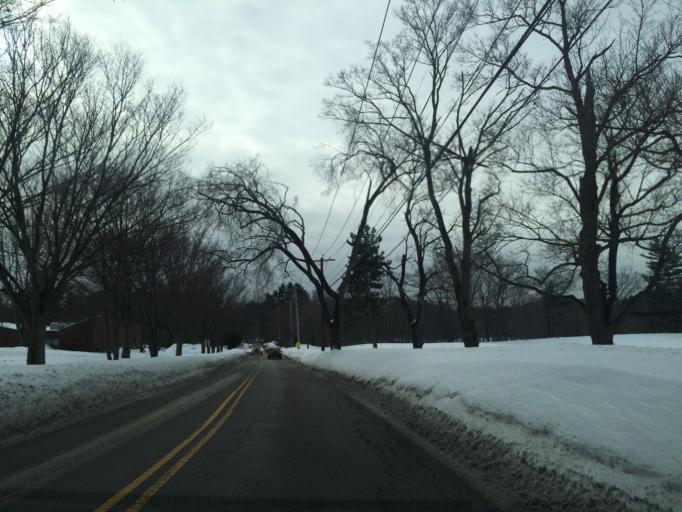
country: US
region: Massachusetts
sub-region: Norfolk County
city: Wellesley
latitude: 42.3326
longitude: -71.2688
